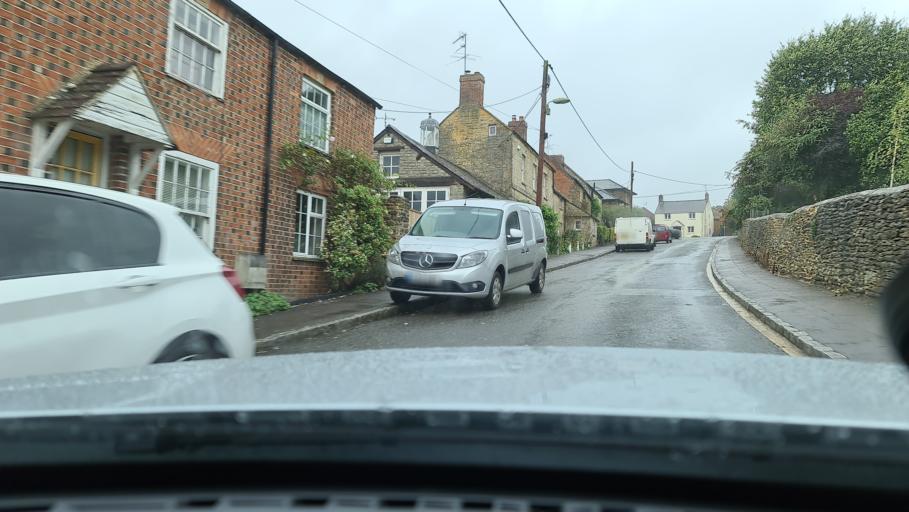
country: GB
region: England
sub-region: Oxfordshire
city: Somerton
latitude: 51.9282
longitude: -1.3087
